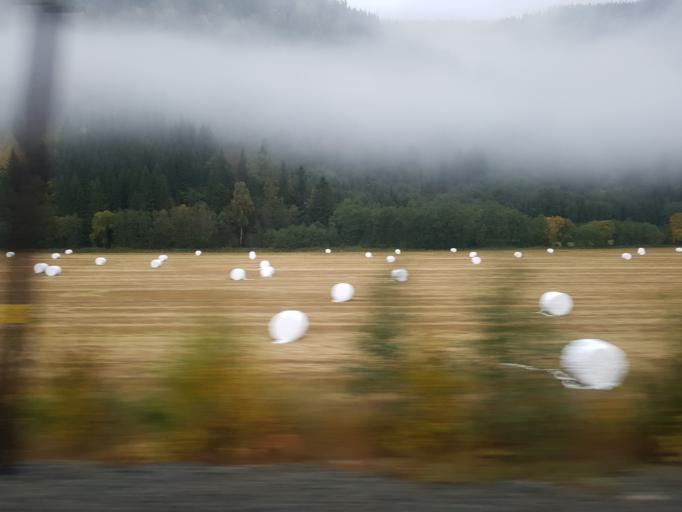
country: NO
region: Sor-Trondelag
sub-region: Melhus
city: Melhus
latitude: 63.2607
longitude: 10.2804
